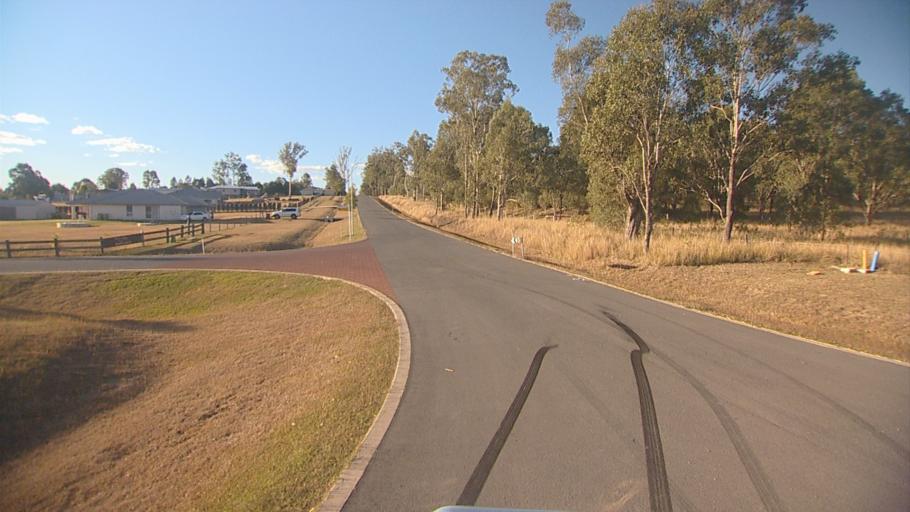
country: AU
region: Queensland
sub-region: Logan
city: Cedar Vale
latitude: -27.8747
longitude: 152.9739
